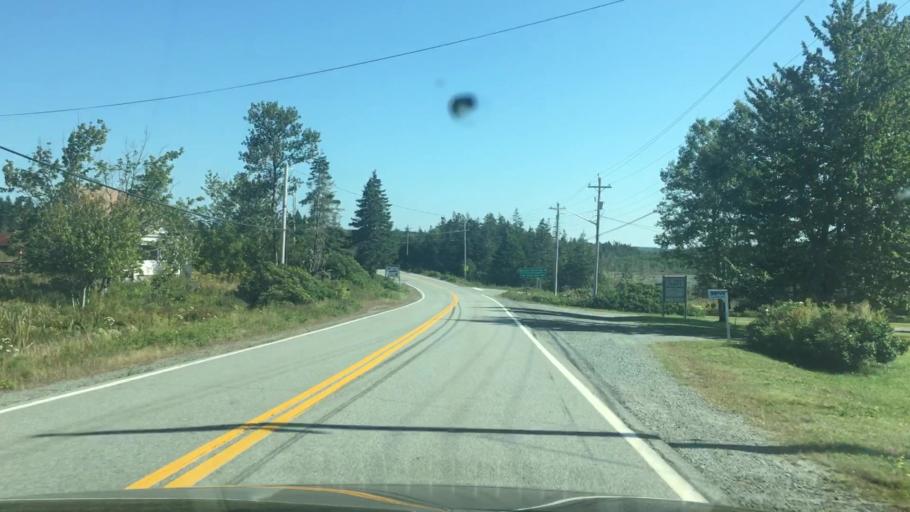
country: CA
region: Nova Scotia
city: New Glasgow
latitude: 44.8045
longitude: -62.6949
